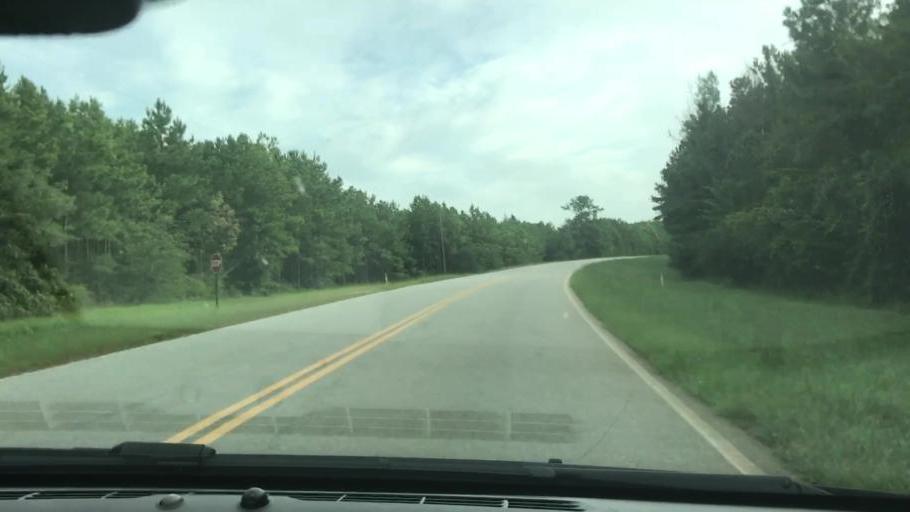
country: US
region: Georgia
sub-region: Stewart County
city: Lumpkin
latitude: 32.0162
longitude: -84.9304
